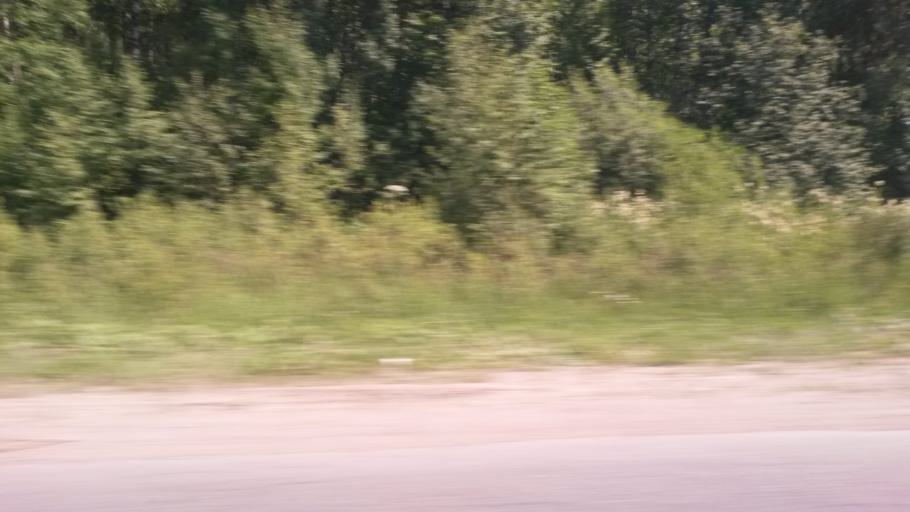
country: RU
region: Ivanovo
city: Rodniki
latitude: 57.1113
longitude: 41.7826
